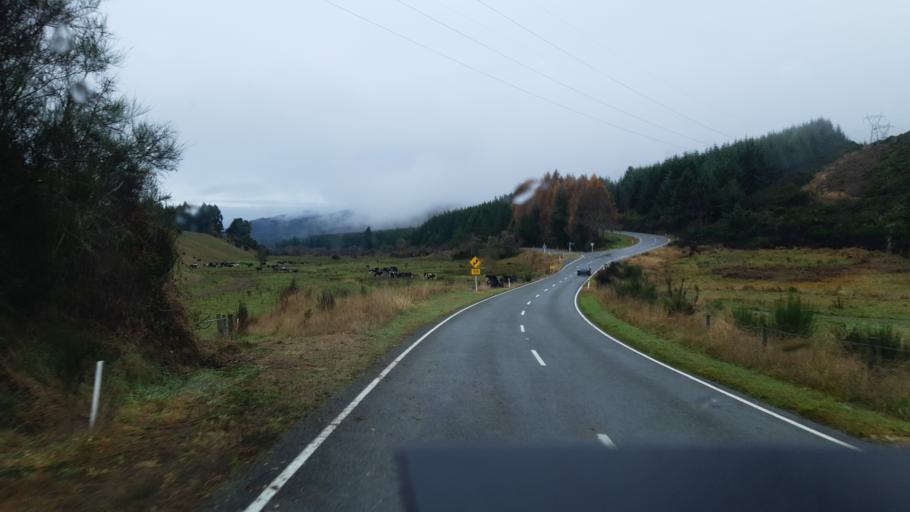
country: NZ
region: Tasman
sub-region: Tasman District
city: Wakefield
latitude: -41.6699
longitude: 172.8747
